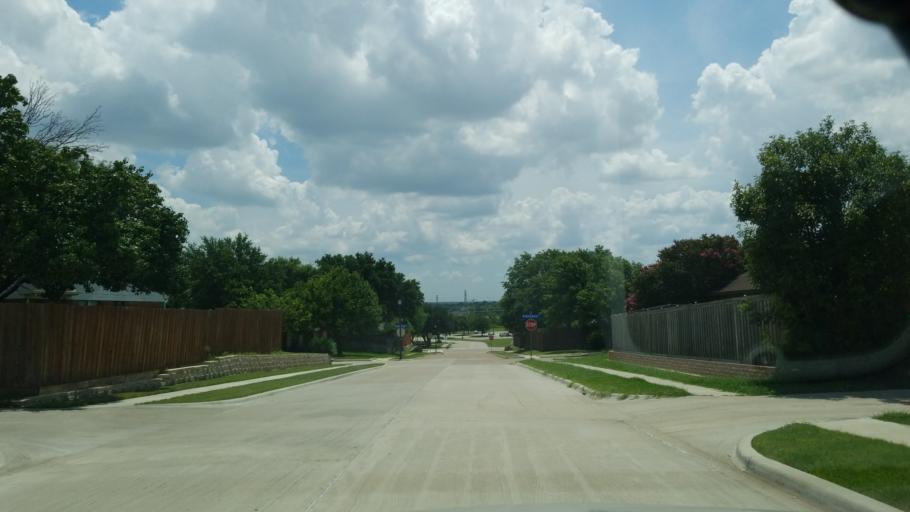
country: US
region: Texas
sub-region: Dallas County
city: Coppell
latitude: 32.9644
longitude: -96.9606
